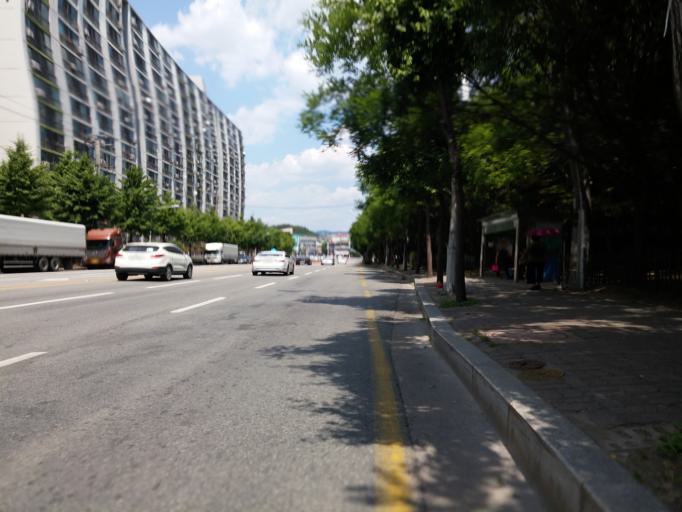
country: KR
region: Chungcheongbuk-do
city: Cheongju-si
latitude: 36.6276
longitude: 127.4377
